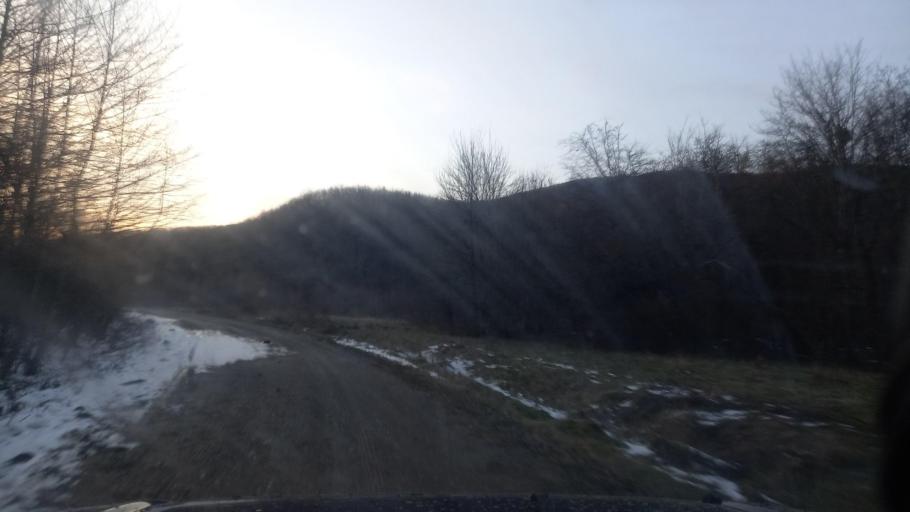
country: RU
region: Krasnodarskiy
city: Smolenskaya
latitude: 44.6235
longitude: 38.8228
